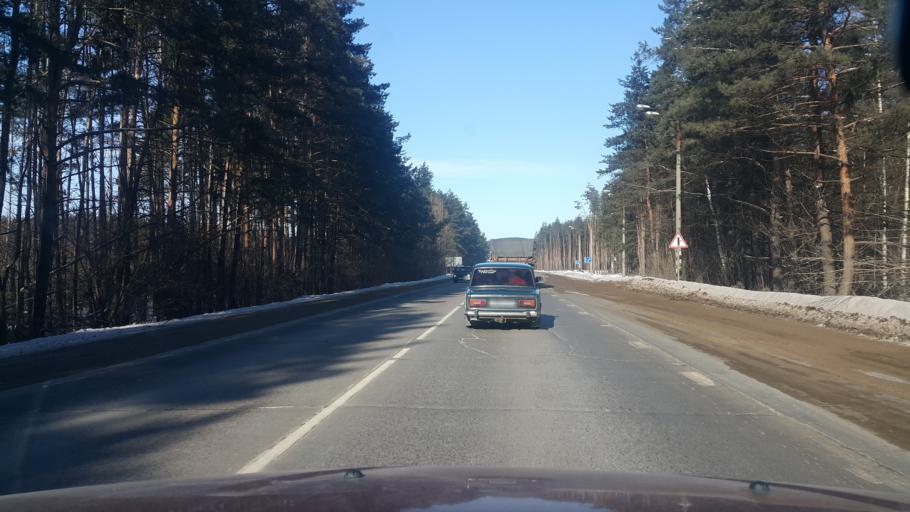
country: RU
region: Tambov
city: Pokrovo-Prigorodnoye
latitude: 52.5893
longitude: 41.3488
